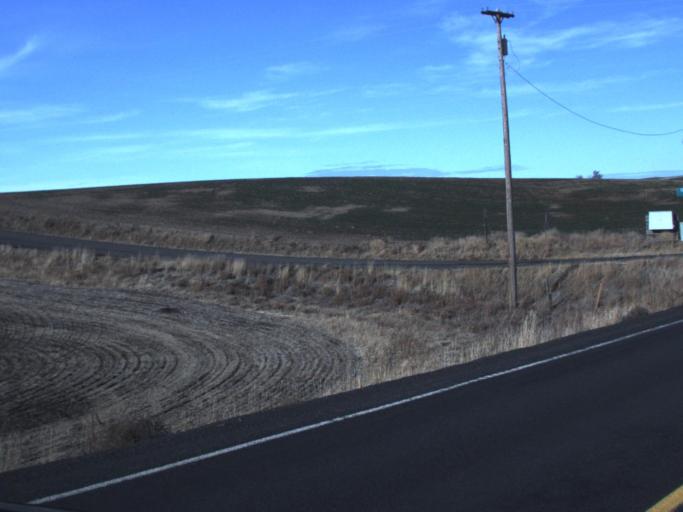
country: US
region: Washington
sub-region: Lincoln County
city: Davenport
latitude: 47.7010
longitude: -118.1410
